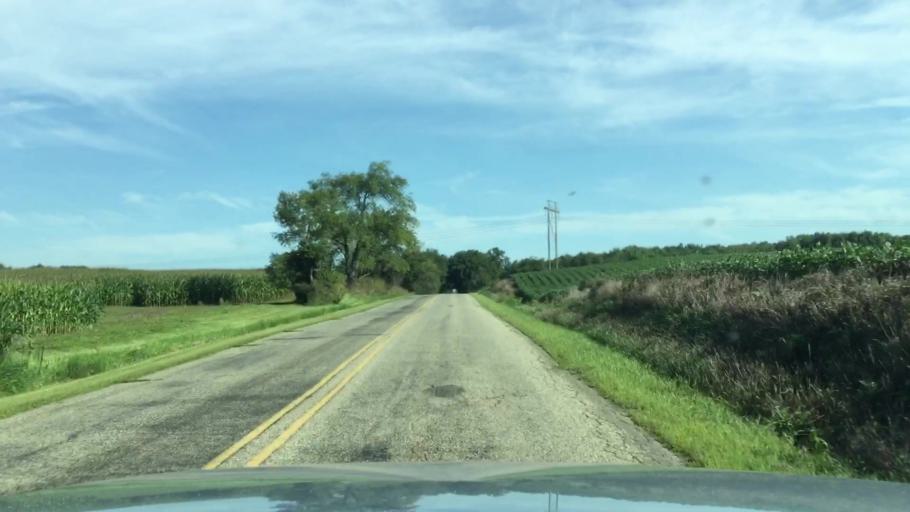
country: US
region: Michigan
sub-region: Lenawee County
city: Hudson
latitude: 41.9167
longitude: -84.4204
